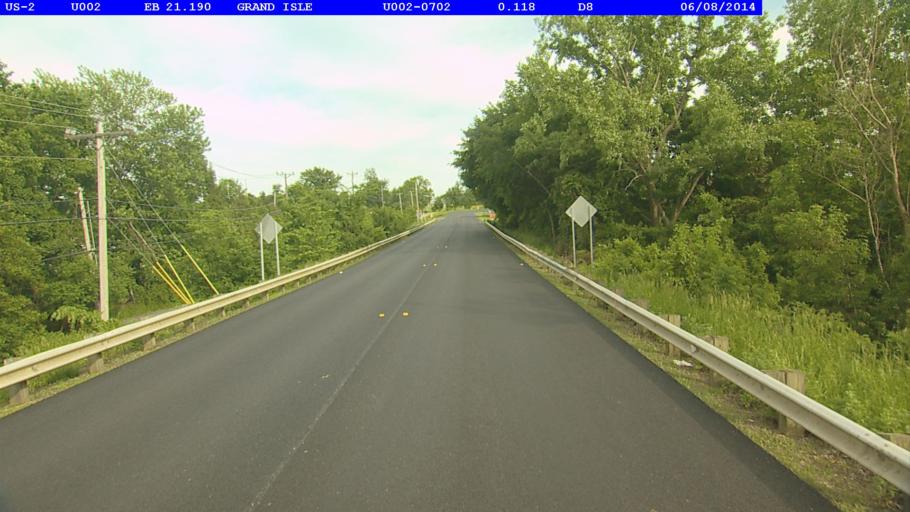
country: US
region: Vermont
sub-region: Grand Isle County
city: North Hero
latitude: 44.7648
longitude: -73.2884
